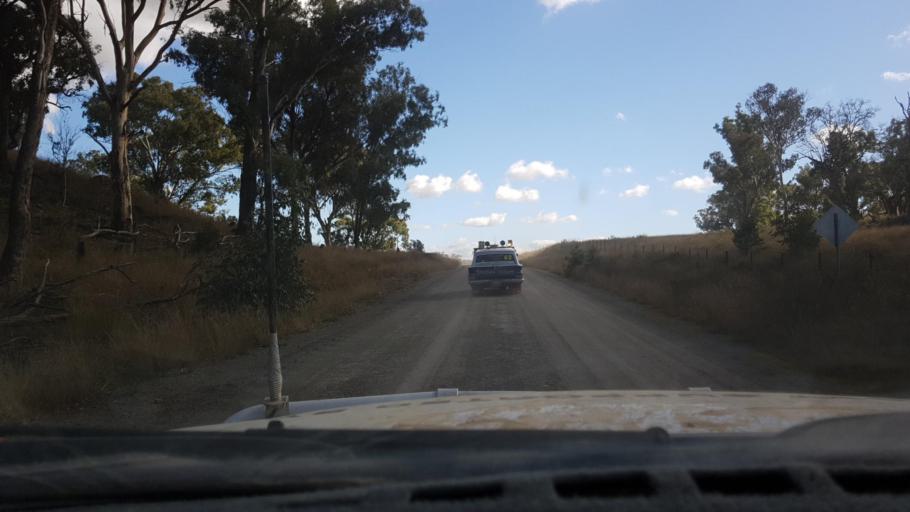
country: AU
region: New South Wales
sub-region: Tamworth Municipality
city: Manilla
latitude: -30.6084
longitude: 150.5045
